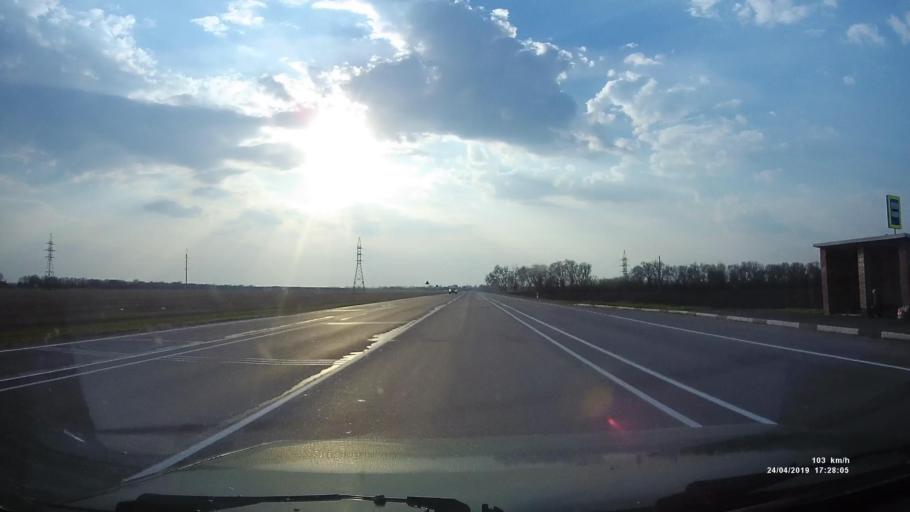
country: RU
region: Rostov
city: Tselina
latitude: 46.5309
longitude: 41.1850
